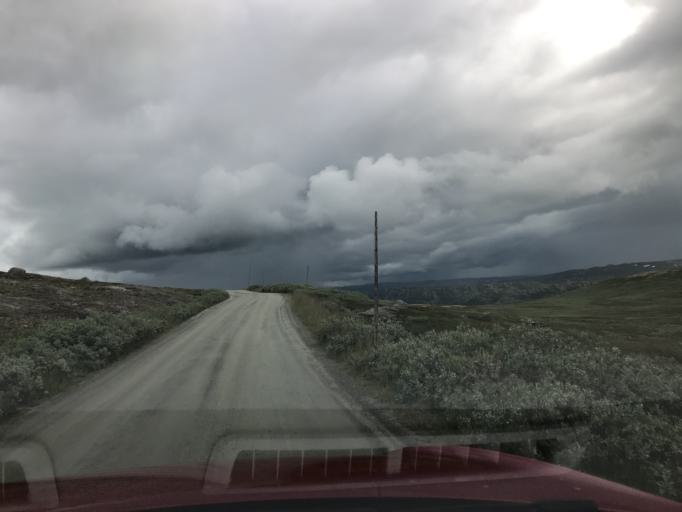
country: NO
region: Buskerud
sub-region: Hol
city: Geilo
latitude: 60.5472
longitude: 8.1012
